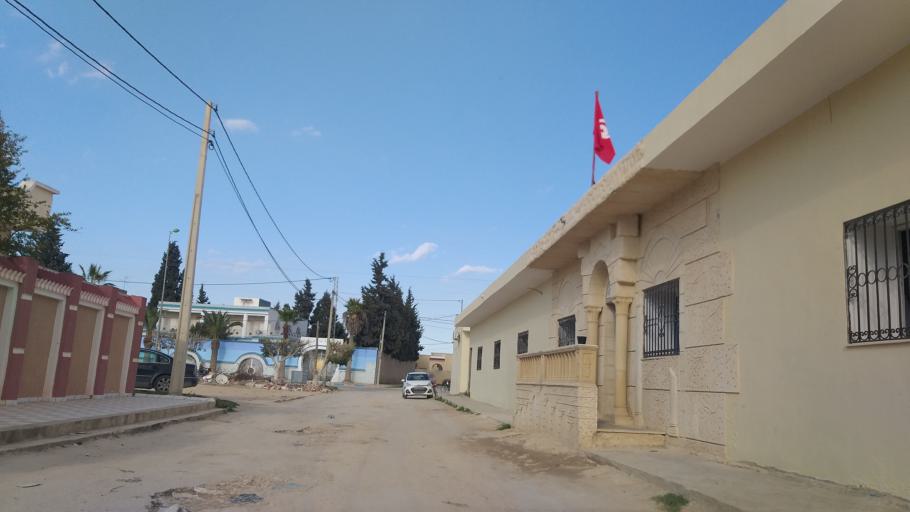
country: TN
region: Al Mahdiyah
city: El Jem
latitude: 35.3064
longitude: 10.7002
